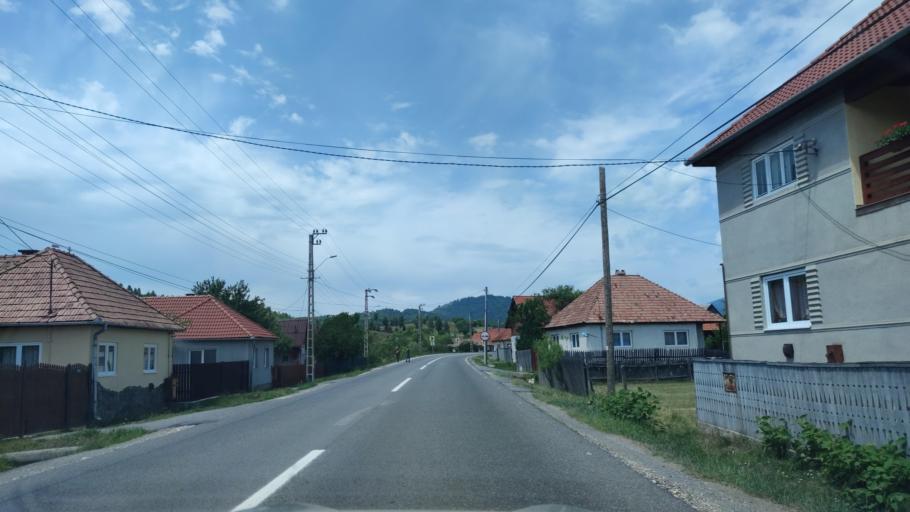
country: RO
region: Harghita
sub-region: Comuna Sandominic
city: Sandominic
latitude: 46.5933
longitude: 25.7632
